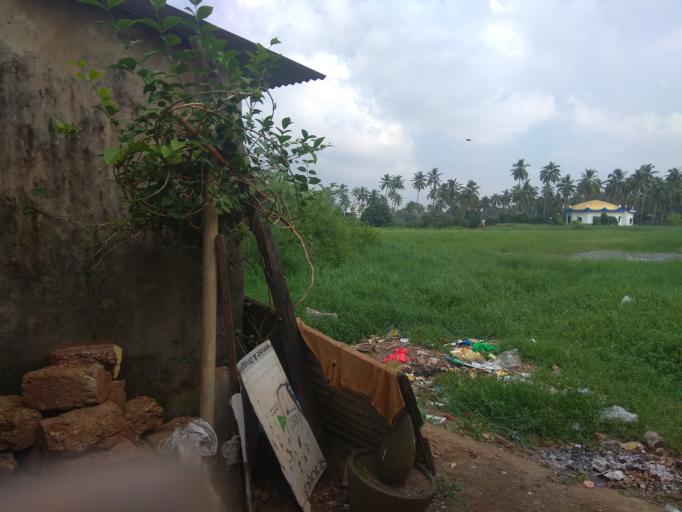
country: IN
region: Goa
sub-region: North Goa
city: Panaji
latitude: 15.4793
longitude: 73.8159
